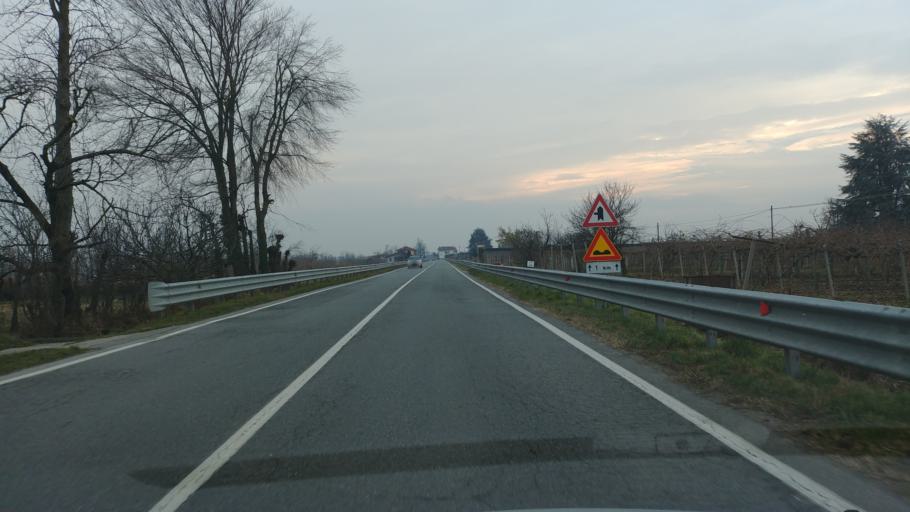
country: IT
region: Piedmont
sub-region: Provincia di Cuneo
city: Sant'Albano Stura
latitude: 44.5066
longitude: 7.6825
